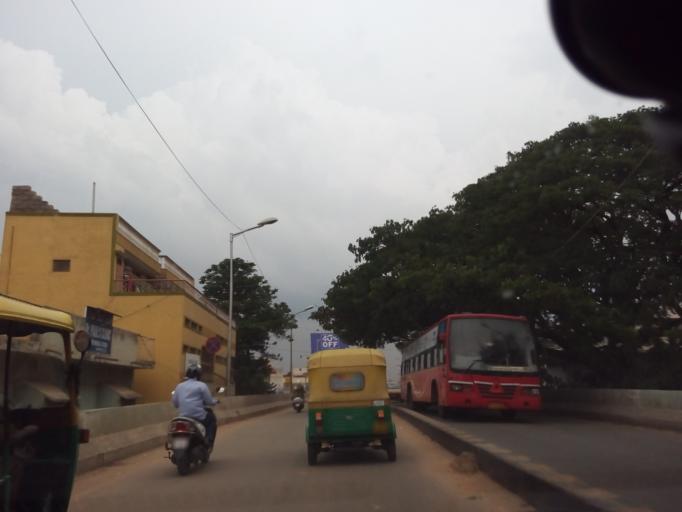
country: IN
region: Karnataka
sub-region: Bangalore Urban
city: Bangalore
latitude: 13.0068
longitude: 77.6213
